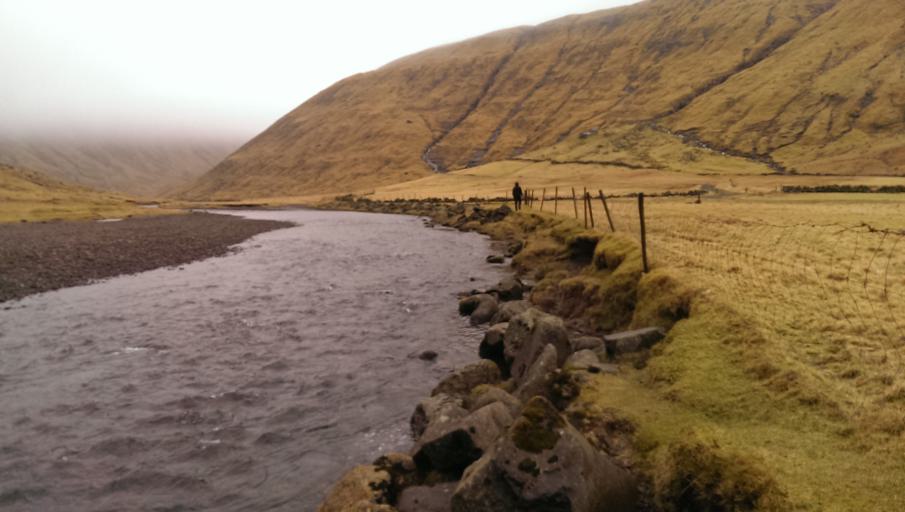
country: FO
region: Streymoy
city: Kollafjordhur
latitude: 62.1333
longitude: -7.0234
